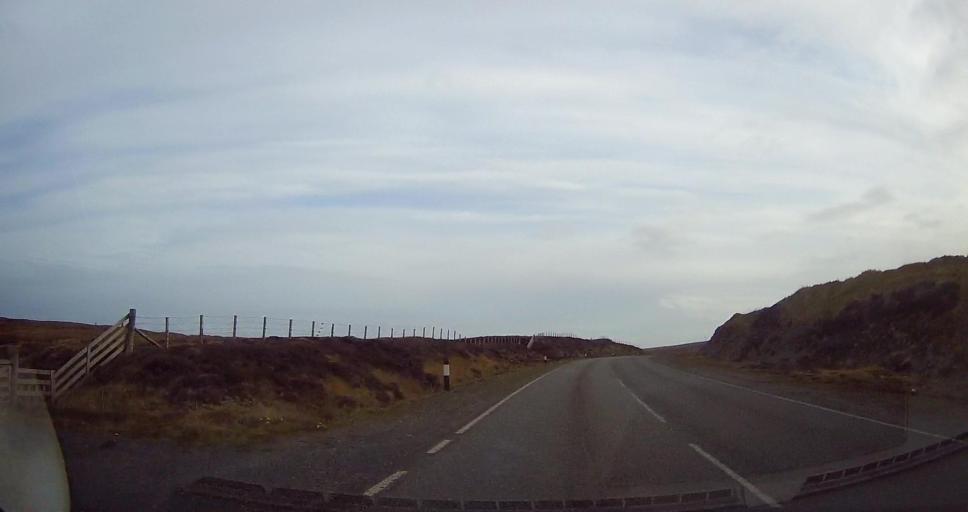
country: GB
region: Scotland
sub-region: Shetland Islands
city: Sandwick
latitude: 60.0903
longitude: -1.2283
